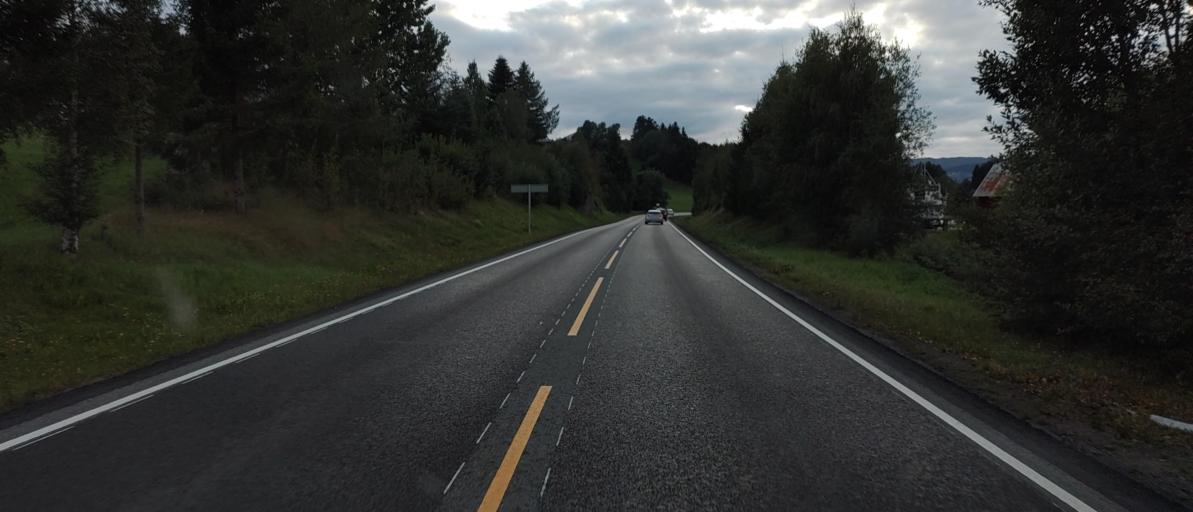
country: NO
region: More og Romsdal
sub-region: Molde
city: Hjelset
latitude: 62.7319
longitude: 7.3375
